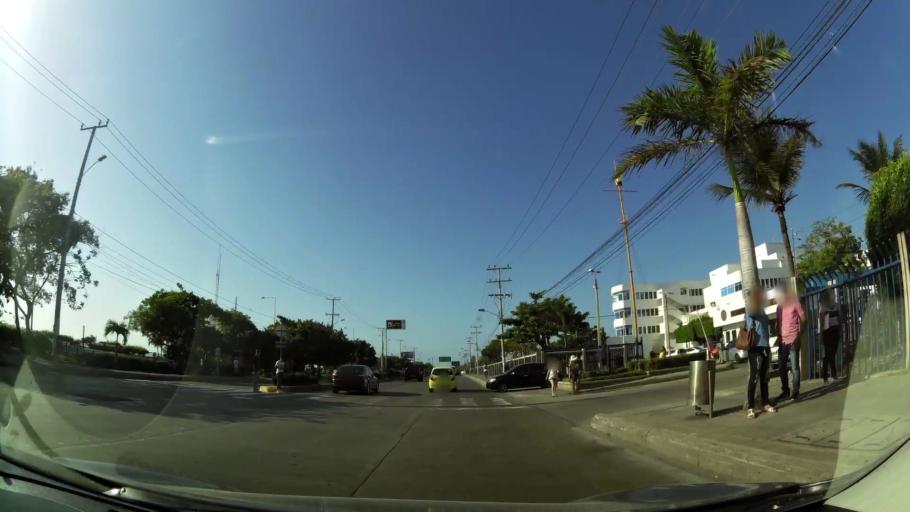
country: CO
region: Bolivar
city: Cartagena
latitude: 10.4158
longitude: -75.5509
